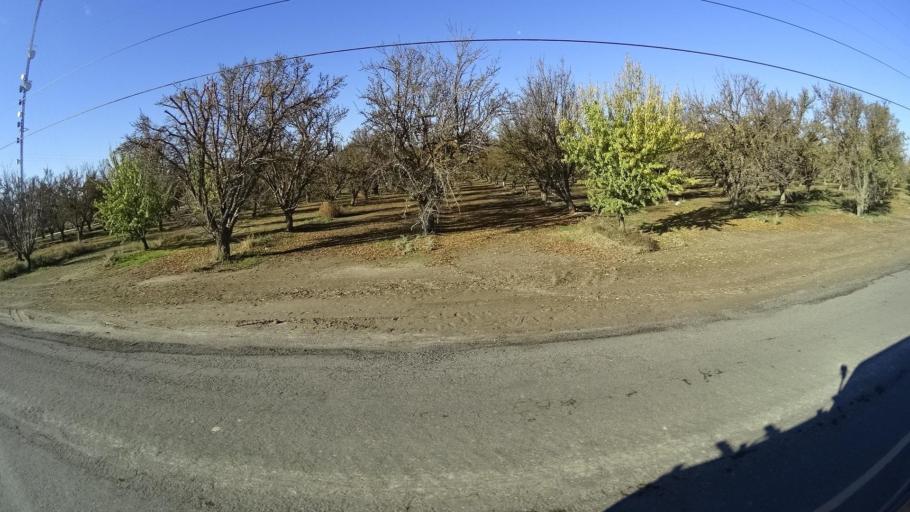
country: US
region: California
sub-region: Kern County
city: Delano
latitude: 35.7543
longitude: -119.3118
